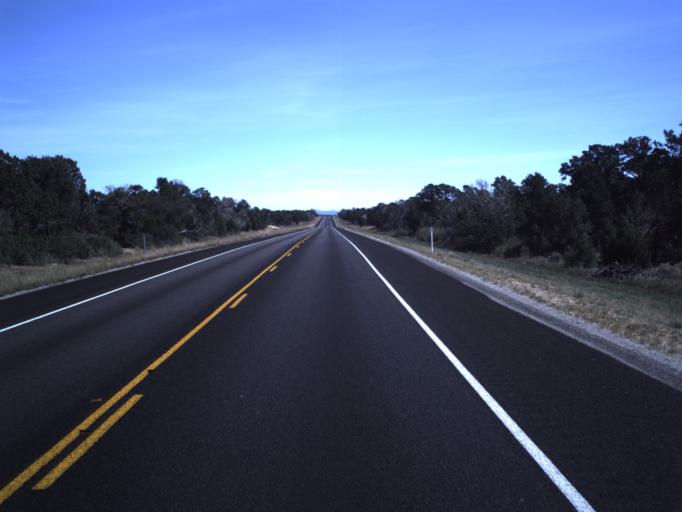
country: US
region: Utah
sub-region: San Juan County
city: Monticello
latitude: 37.8594
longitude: -109.2050
